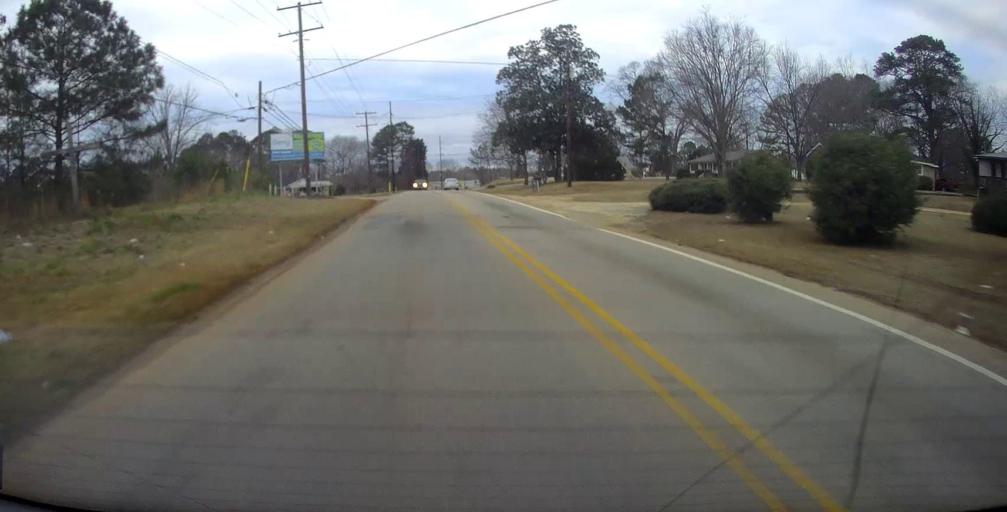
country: US
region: Alabama
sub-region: Chambers County
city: Huguley
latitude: 32.8308
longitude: -85.2255
